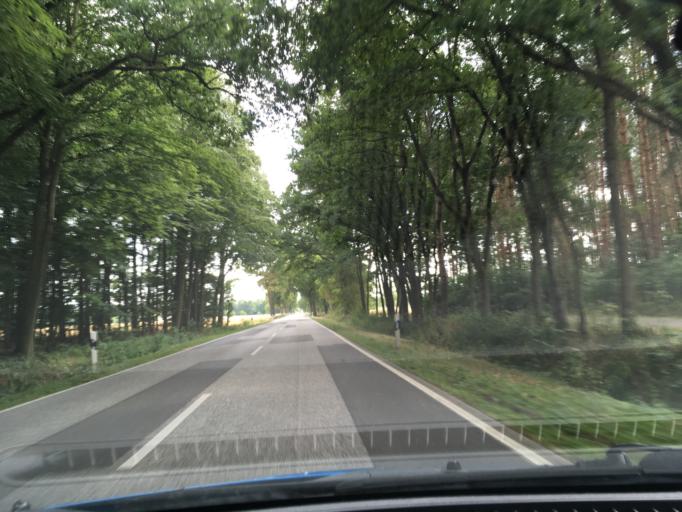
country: DE
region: Mecklenburg-Vorpommern
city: Lubtheen
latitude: 53.3446
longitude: 11.0825
